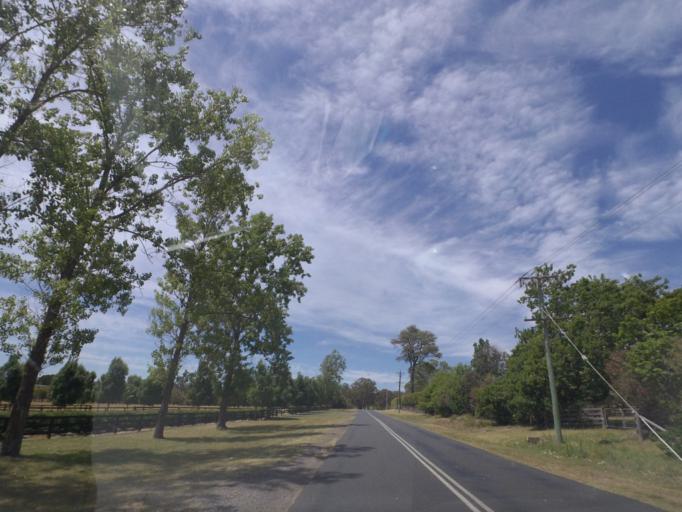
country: AU
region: New South Wales
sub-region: Wingecarribee
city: Colo Vale
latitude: -34.4091
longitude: 150.5248
